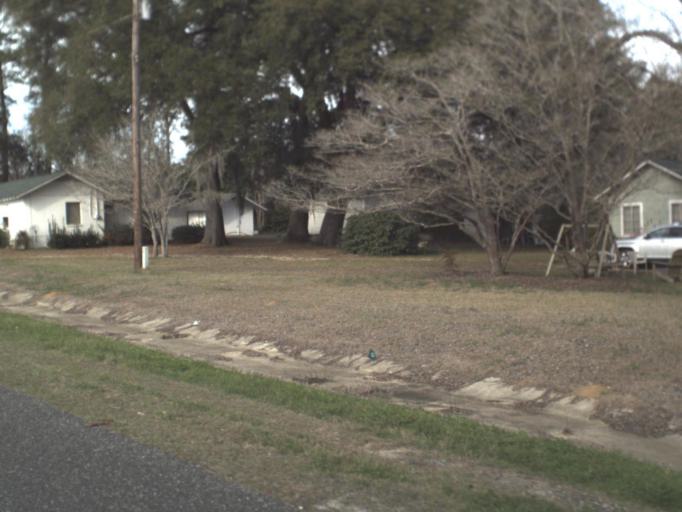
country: US
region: Florida
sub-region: Jefferson County
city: Monticello
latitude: 30.5808
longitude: -83.8700
